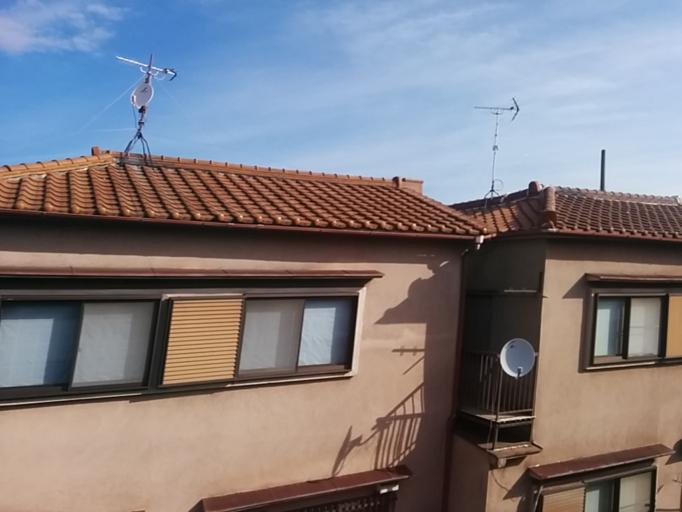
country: JP
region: Nara
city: Nara-shi
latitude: 34.6864
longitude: 135.8047
